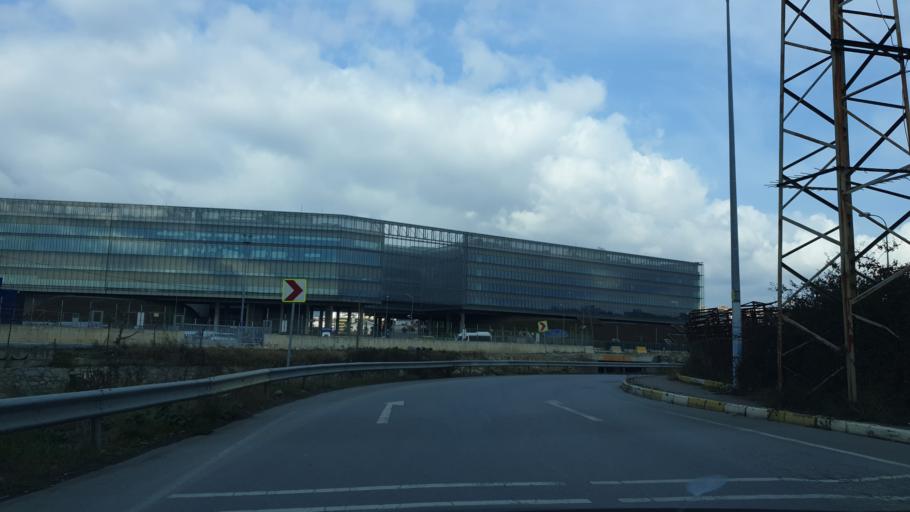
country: TR
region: Istanbul
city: Pendik
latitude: 40.8664
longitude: 29.2790
